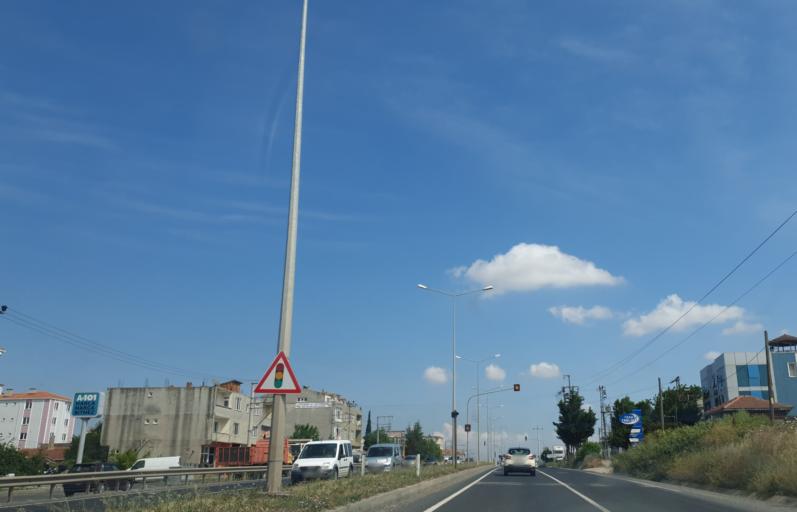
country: TR
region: Tekirdag
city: Marmaracik
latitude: 41.2356
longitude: 27.7045
